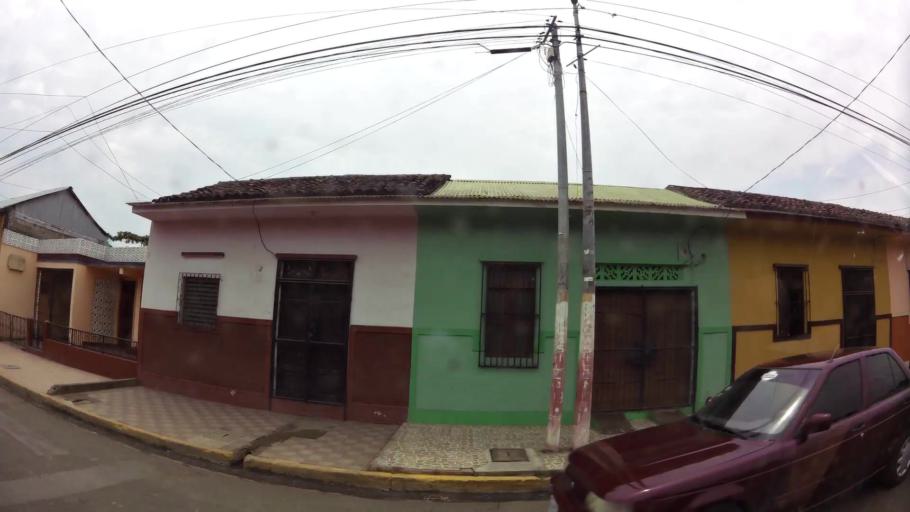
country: NI
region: Granada
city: Granada
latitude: 11.9232
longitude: -85.9551
